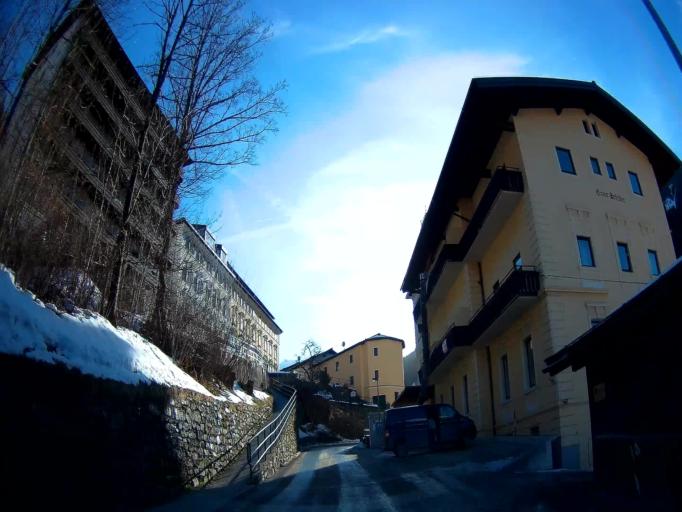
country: AT
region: Salzburg
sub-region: Politischer Bezirk Sankt Johann im Pongau
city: Bad Gastein
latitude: 47.1185
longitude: 13.1384
